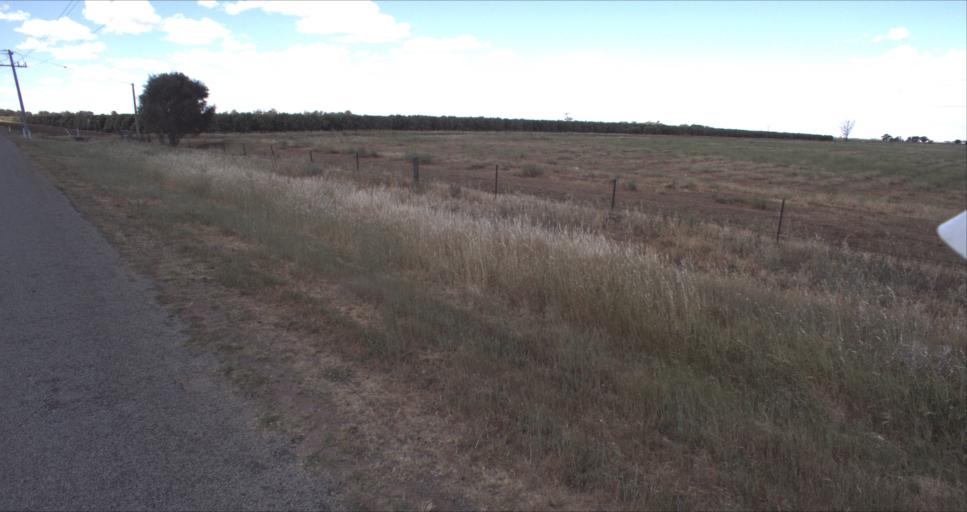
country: AU
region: New South Wales
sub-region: Leeton
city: Leeton
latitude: -34.5253
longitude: 146.2215
